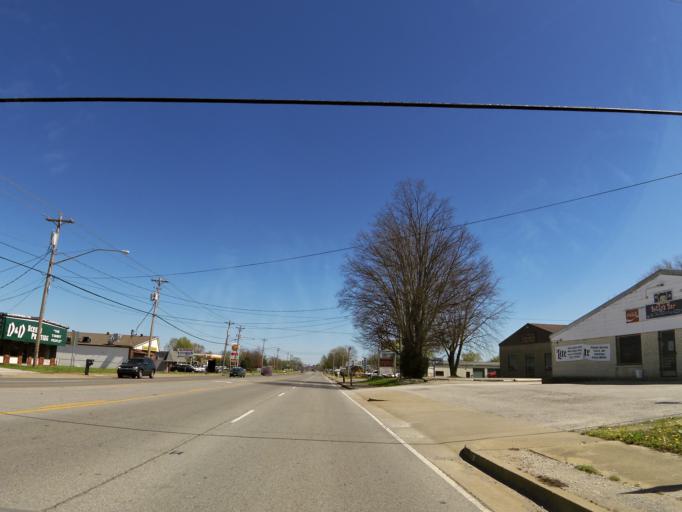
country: US
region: Kentucky
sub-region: Warren County
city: Bowling Green
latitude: 36.9650
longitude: -86.4852
